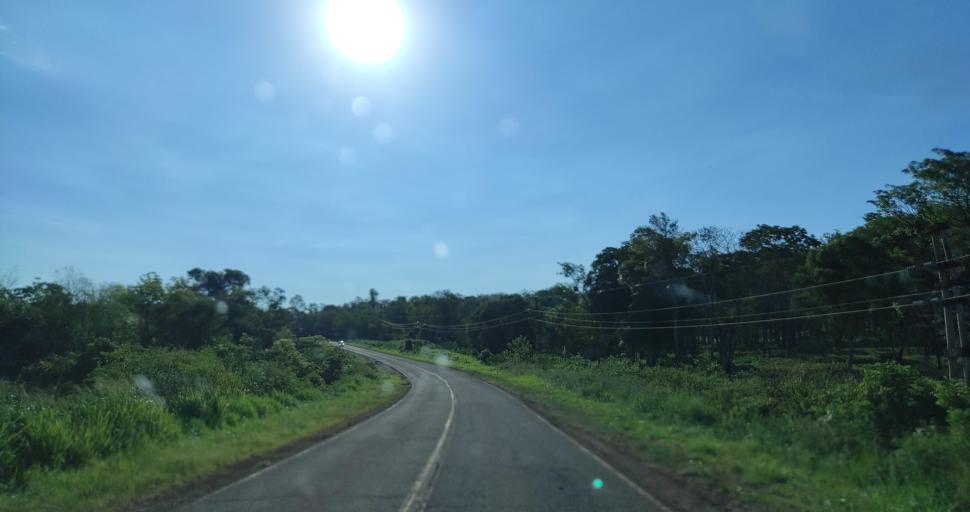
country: AR
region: Misiones
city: San Vicente
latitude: -26.3728
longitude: -54.3182
